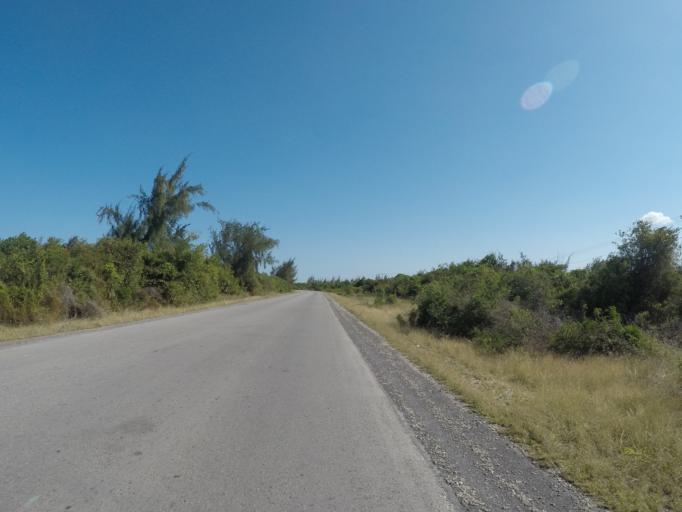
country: TZ
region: Zanzibar Central/South
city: Nganane
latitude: -6.2119
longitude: 39.5300
